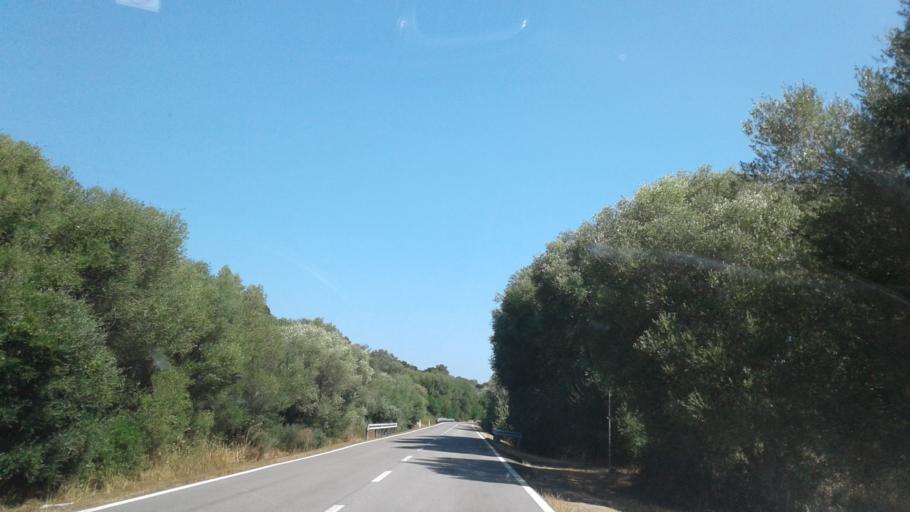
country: IT
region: Sardinia
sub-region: Provincia di Olbia-Tempio
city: Palau
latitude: 41.1524
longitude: 9.3142
